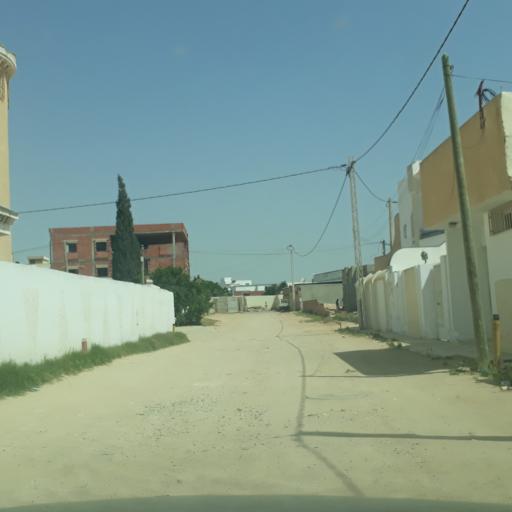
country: TN
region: Safaqis
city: Al Qarmadah
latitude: 34.7979
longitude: 10.7641
